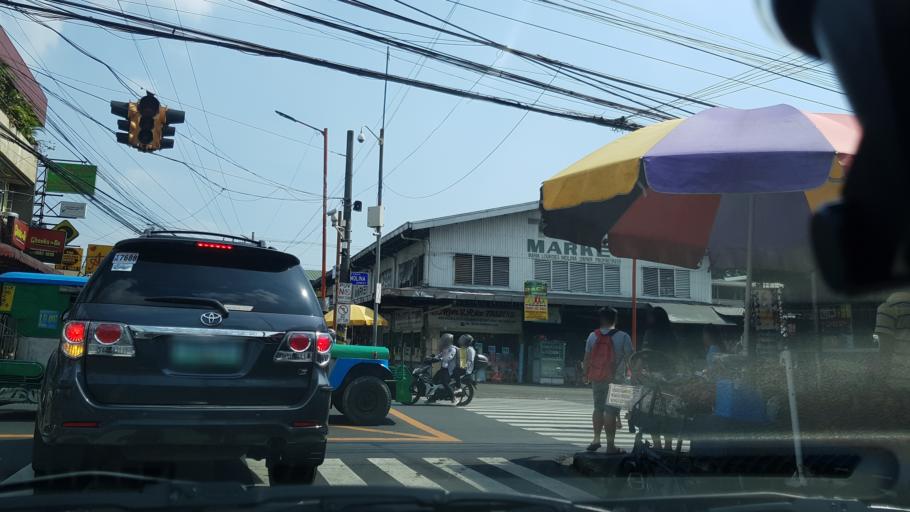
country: PH
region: Calabarzon
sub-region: Province of Rizal
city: Antipolo
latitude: 14.6595
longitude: 121.1133
